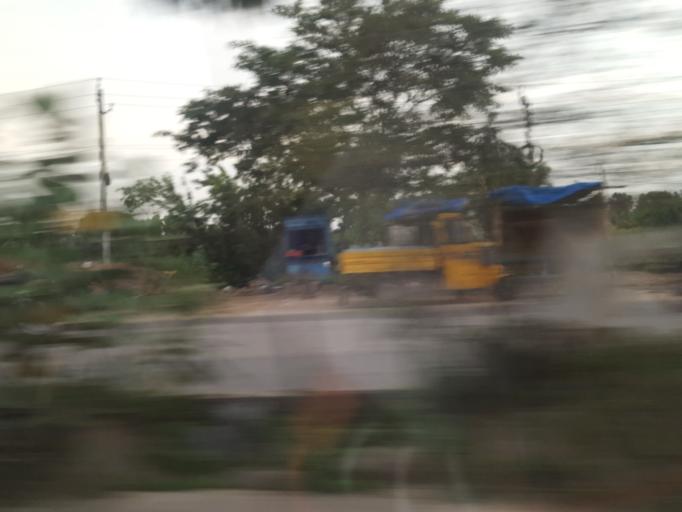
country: IN
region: Telangana
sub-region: Medak
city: Serilingampalle
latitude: 17.5160
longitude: 78.3580
